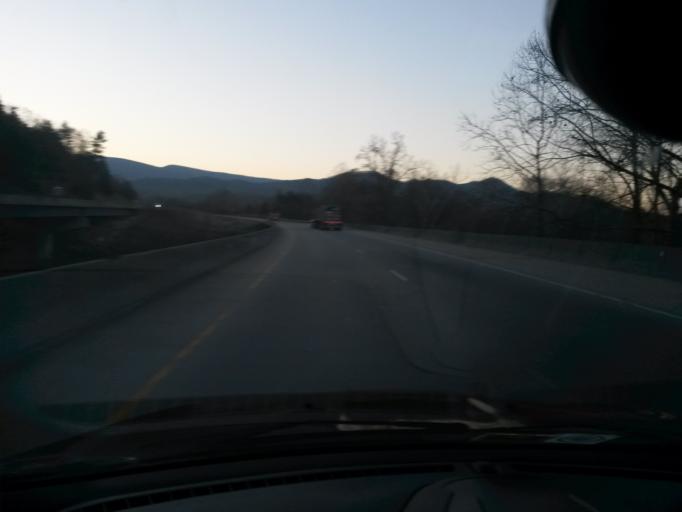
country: US
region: Virginia
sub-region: Alleghany County
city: Clifton Forge
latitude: 37.8080
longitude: -79.7402
